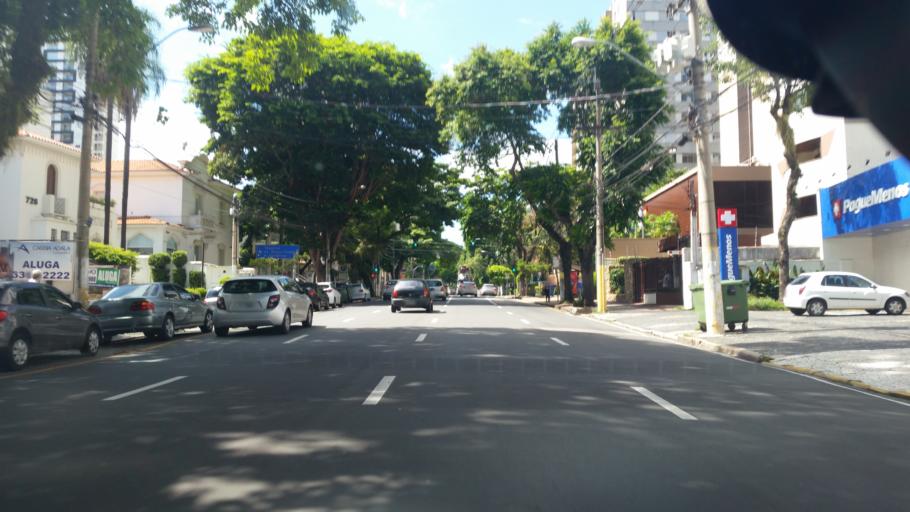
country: BR
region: Sao Paulo
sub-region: Campinas
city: Campinas
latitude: -22.8991
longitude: -47.0555
